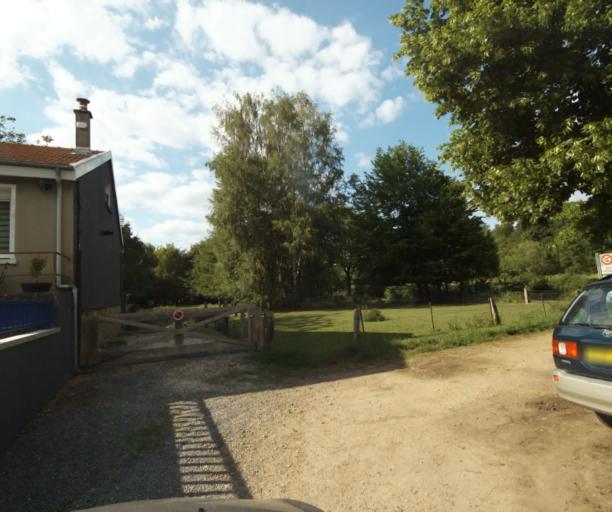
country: FR
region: Champagne-Ardenne
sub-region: Departement des Ardennes
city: Montcy-Notre-Dame
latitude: 49.7789
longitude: 4.7360
